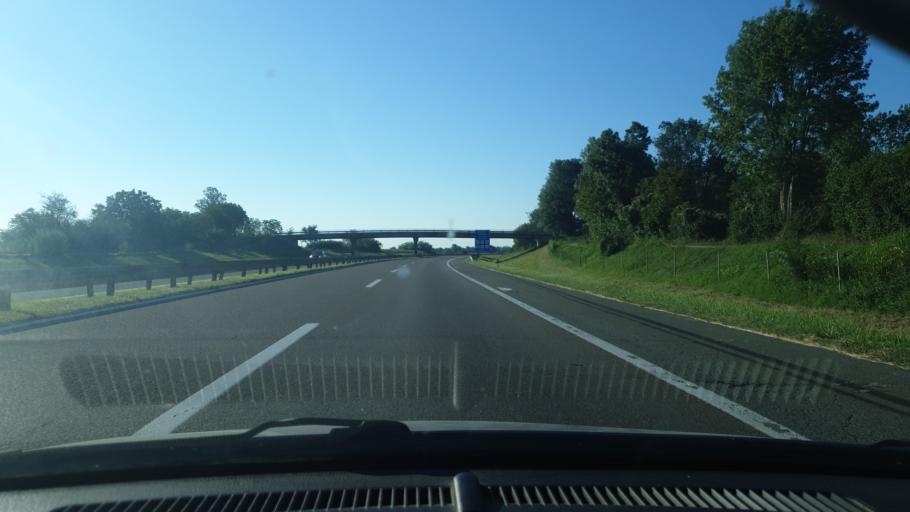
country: RS
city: Lugavcina
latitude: 44.4304
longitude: 21.0546
